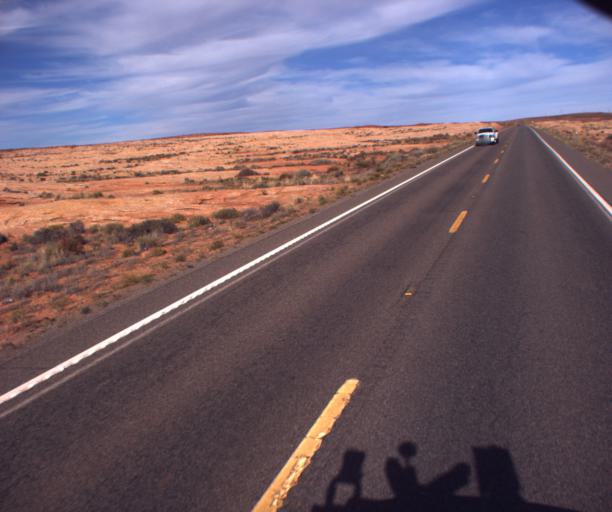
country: US
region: Arizona
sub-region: Navajo County
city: Kayenta
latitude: 36.8881
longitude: -109.8095
